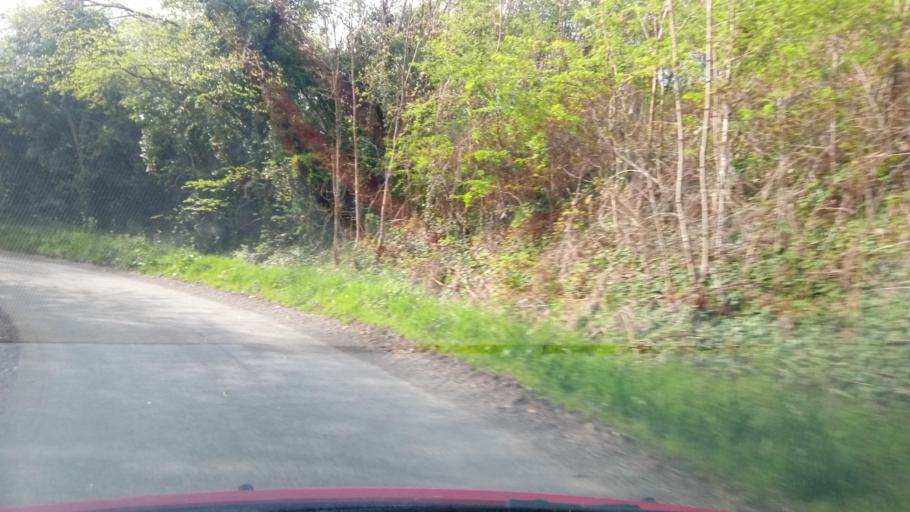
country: GB
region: Scotland
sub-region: The Scottish Borders
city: Saint Boswells
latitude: 55.5165
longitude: -2.6779
